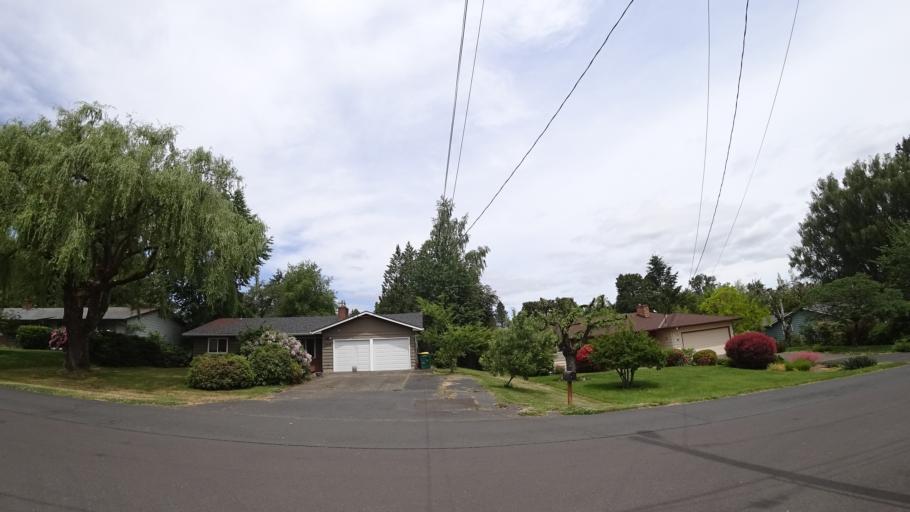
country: US
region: Oregon
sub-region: Washington County
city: Metzger
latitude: 45.4491
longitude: -122.7735
